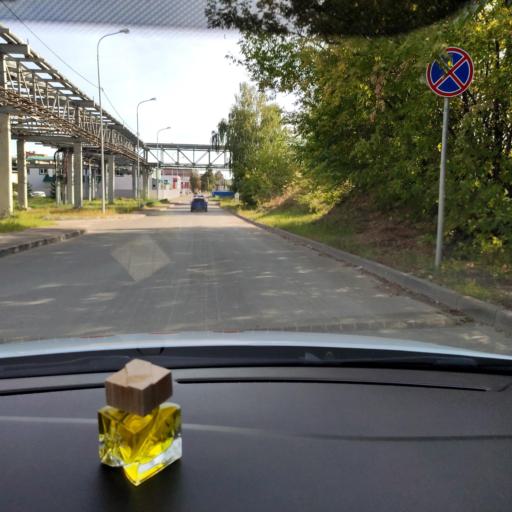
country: RU
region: Tatarstan
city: Staroye Arakchino
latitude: 55.8373
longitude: 49.0486
